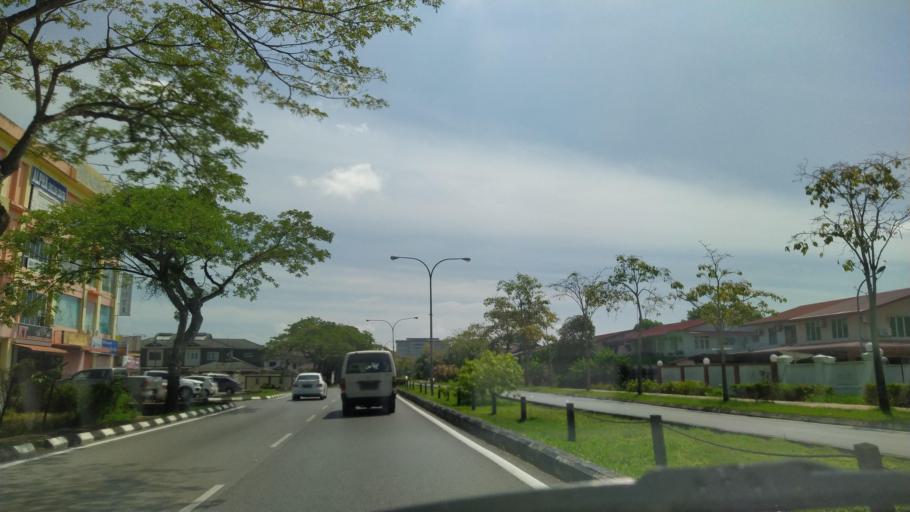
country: MY
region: Sarawak
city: Sibu
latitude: 2.3162
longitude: 111.8376
